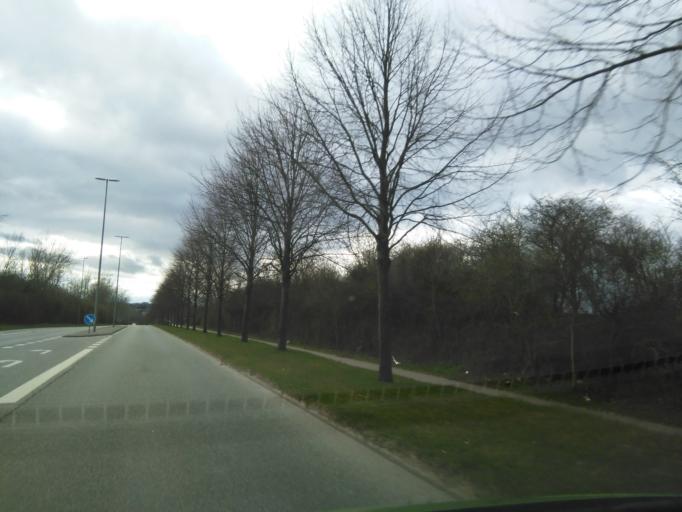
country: DK
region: Central Jutland
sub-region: Arhus Kommune
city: Stavtrup
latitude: 56.1741
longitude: 10.1302
